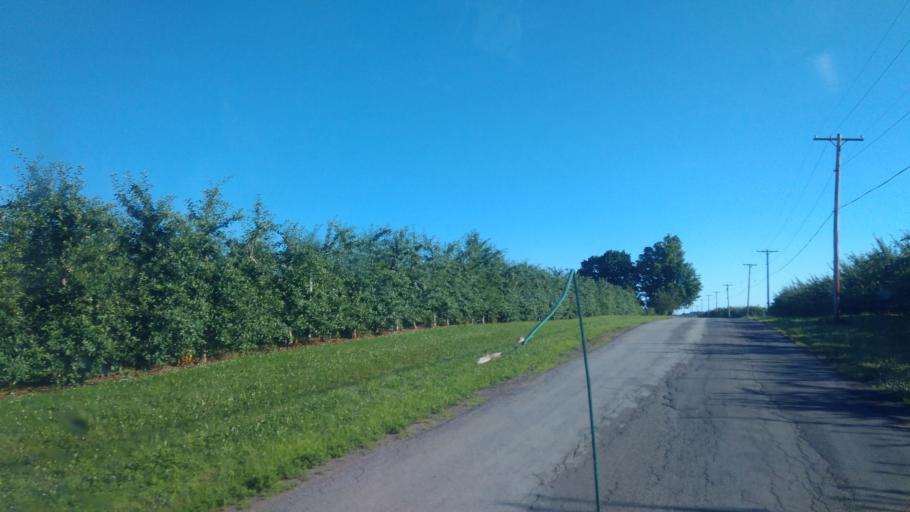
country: US
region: New York
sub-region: Wayne County
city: Sodus
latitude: 43.1770
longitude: -77.0617
